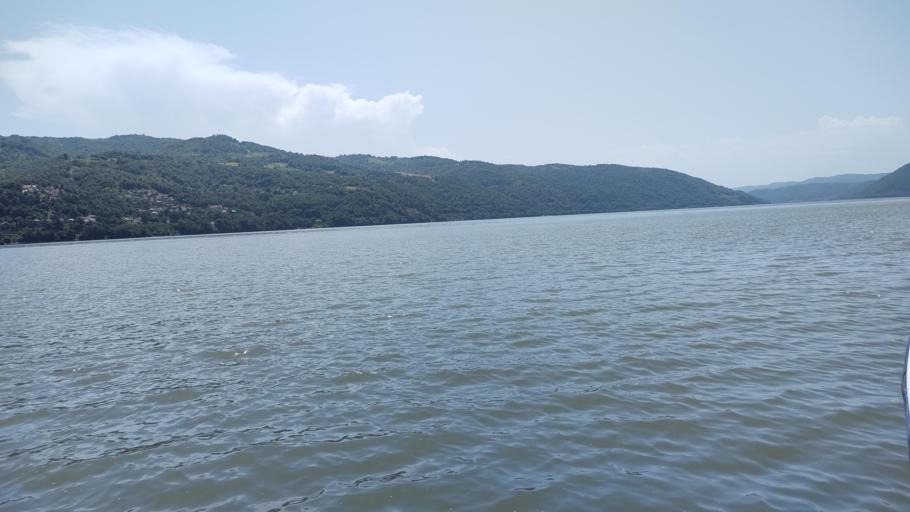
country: RO
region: Mehedinti
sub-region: Comuna Svinita
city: Svinita
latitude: 44.5048
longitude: 22.1923
